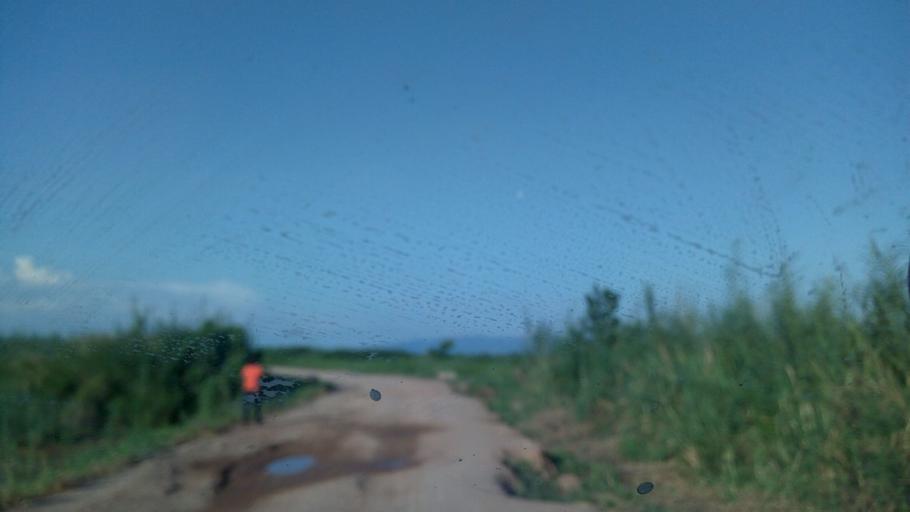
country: BI
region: Bururi
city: Rumonge
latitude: -4.2031
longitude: 29.0456
